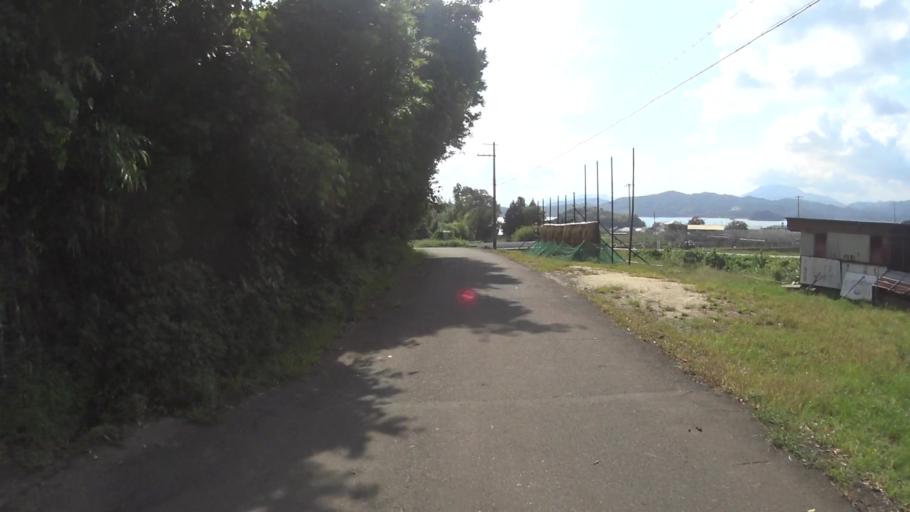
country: JP
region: Kyoto
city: Miyazu
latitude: 35.6106
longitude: 135.2184
